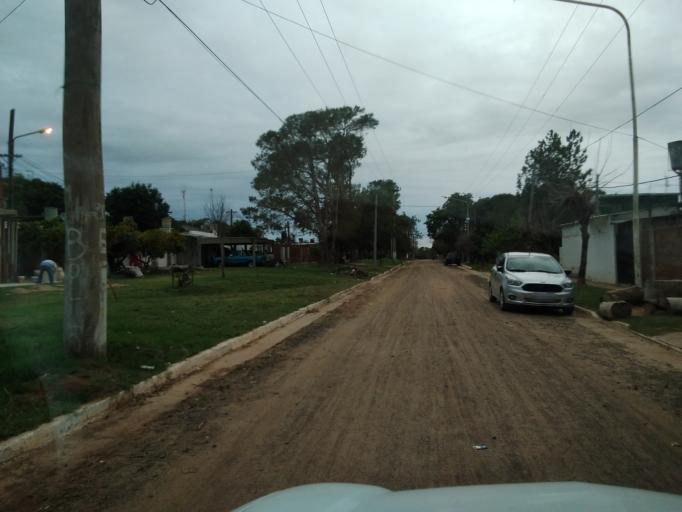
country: AR
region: Corrientes
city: Corrientes
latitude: -27.5068
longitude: -58.7969
